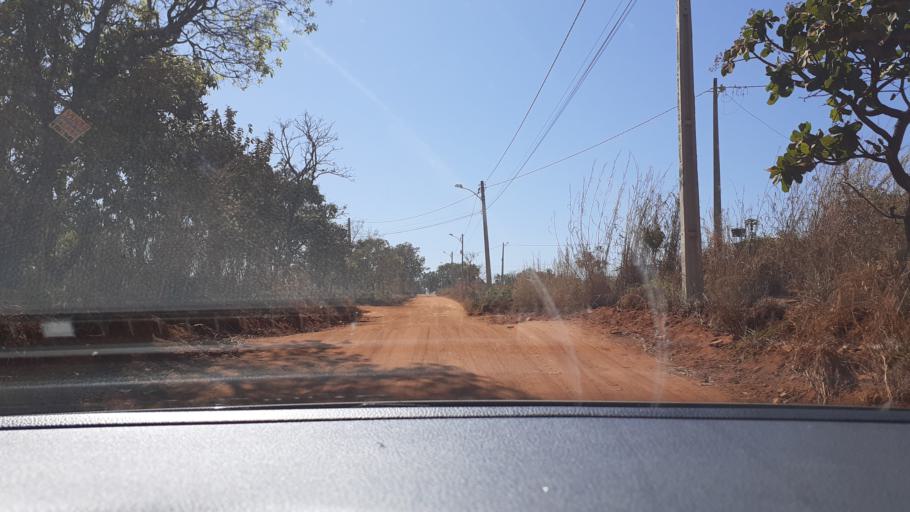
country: BR
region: Goias
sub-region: Aparecida De Goiania
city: Aparecida de Goiania
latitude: -16.8897
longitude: -49.2596
